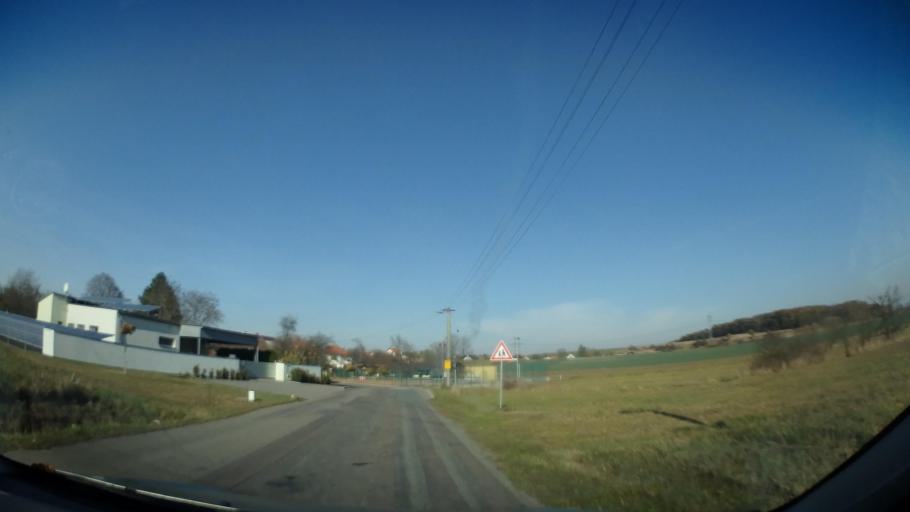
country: CZ
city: Ceske Mezirici
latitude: 50.2483
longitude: 16.0153
